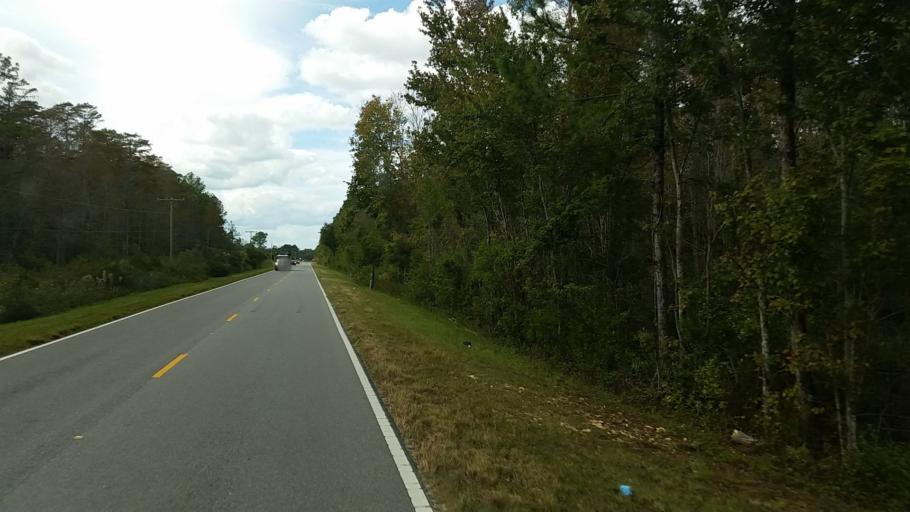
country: US
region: Florida
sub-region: Lake County
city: Four Corners
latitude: 28.3764
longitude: -81.8083
